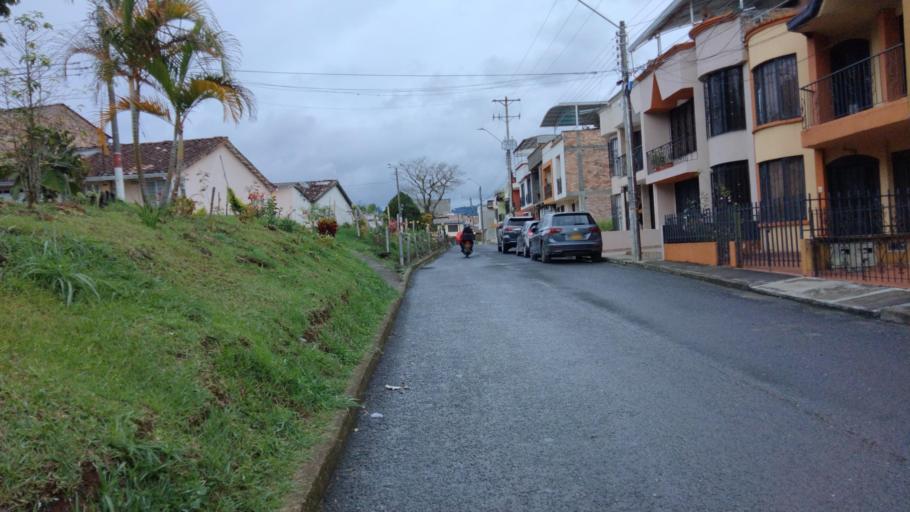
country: CO
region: Cauca
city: Popayan
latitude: 2.4583
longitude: -76.5911
